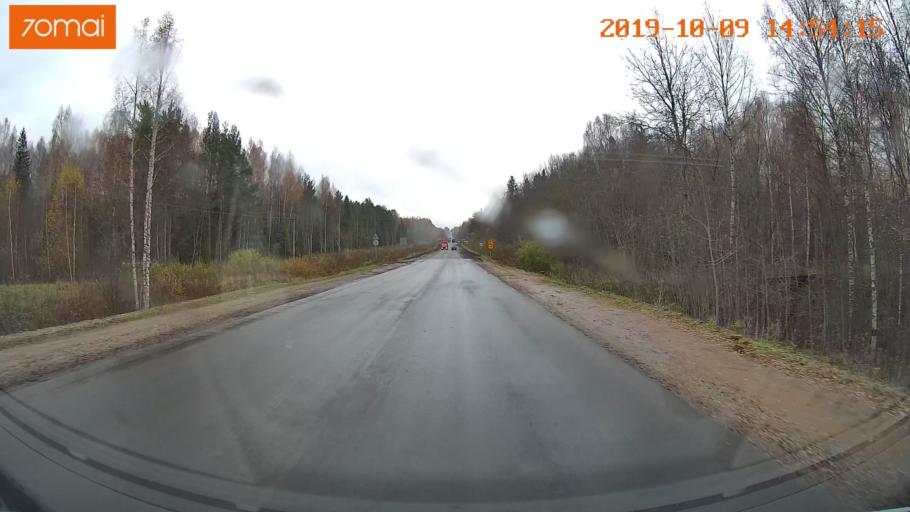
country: RU
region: Kostroma
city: Chistyye Bory
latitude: 58.3586
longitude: 41.6420
